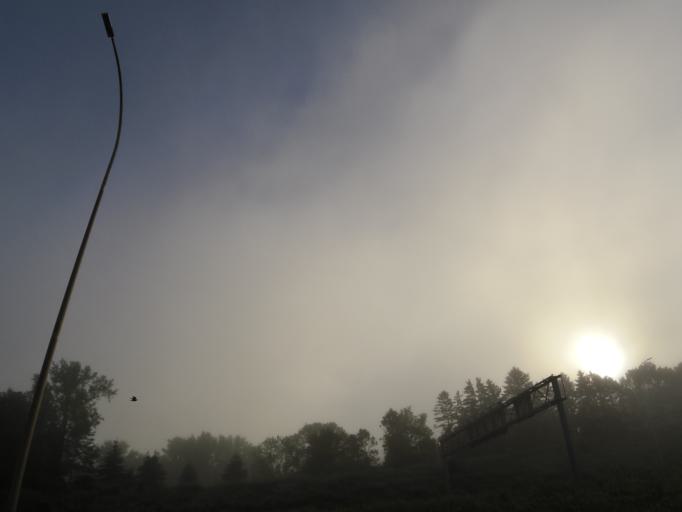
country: US
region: Minnesota
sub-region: Ramsey County
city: Arden Hills
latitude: 45.0649
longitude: -93.1631
